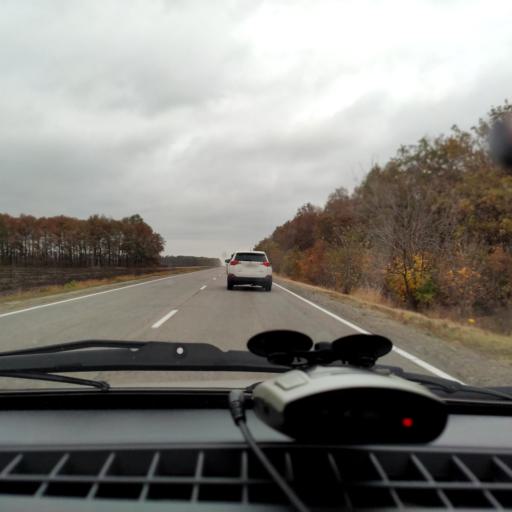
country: RU
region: Voronezj
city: Shilovo
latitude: 51.4184
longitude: 39.0068
